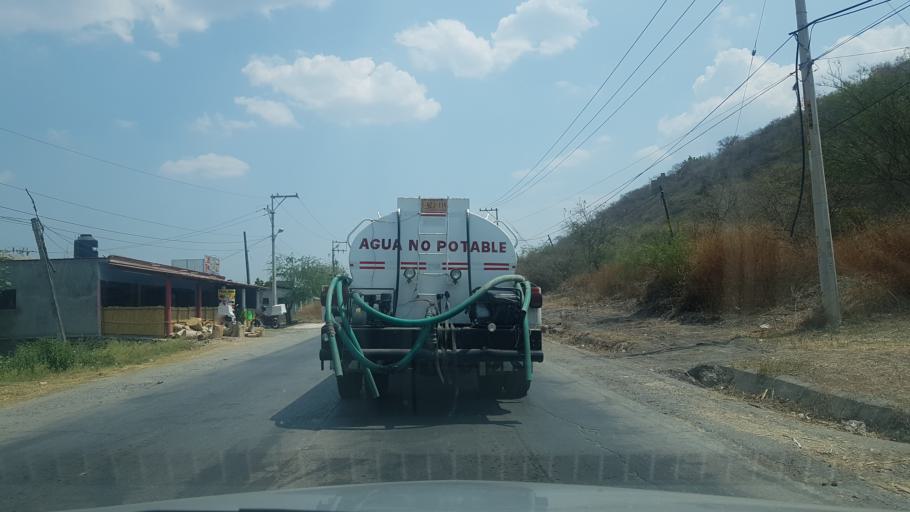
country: MX
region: Morelos
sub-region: Tlaltizapan de Zapata
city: Colonia Palo Prieto (Chipitongo)
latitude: 18.7110
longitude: -99.1172
